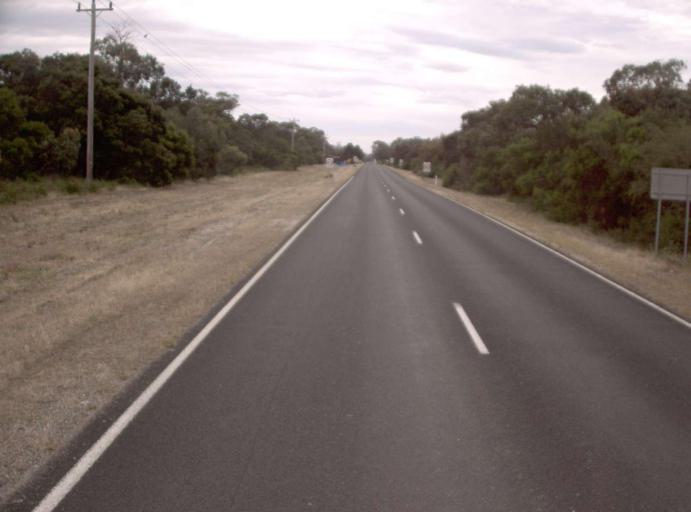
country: AU
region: Victoria
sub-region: East Gippsland
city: Bairnsdale
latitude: -38.0614
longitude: 147.5627
